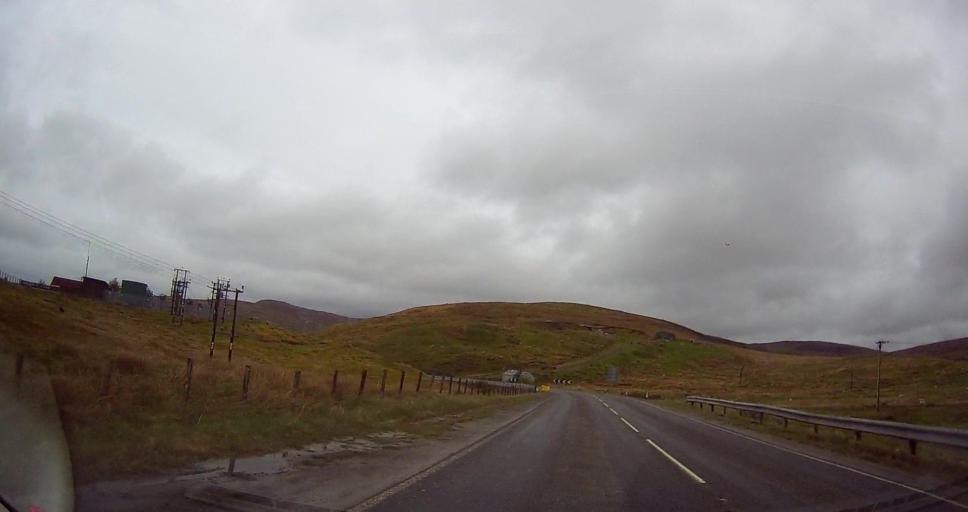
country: GB
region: Scotland
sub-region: Shetland Islands
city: Lerwick
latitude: 60.3487
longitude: -1.2537
